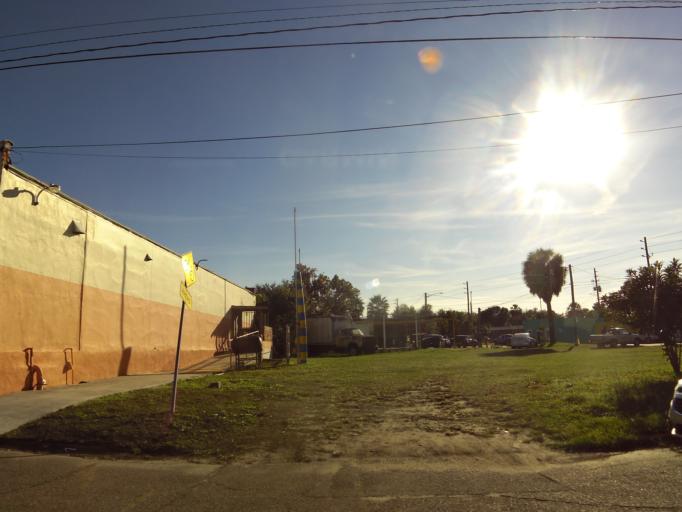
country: US
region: Florida
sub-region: Duval County
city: Jacksonville
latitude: 30.3392
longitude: -81.6752
